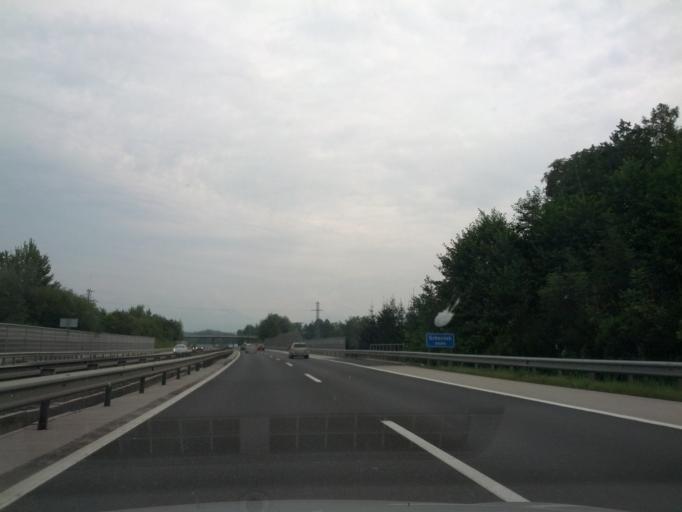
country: SI
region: Dol pri Ljubljani
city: Dol pri Ljubljani
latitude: 46.1096
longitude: 14.6005
